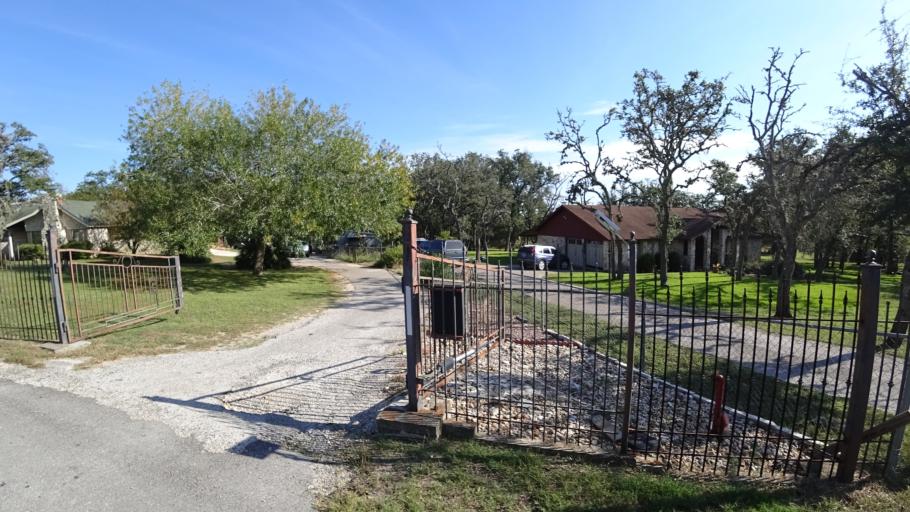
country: US
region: Texas
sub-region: Travis County
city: Bee Cave
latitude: 30.2392
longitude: -97.9374
